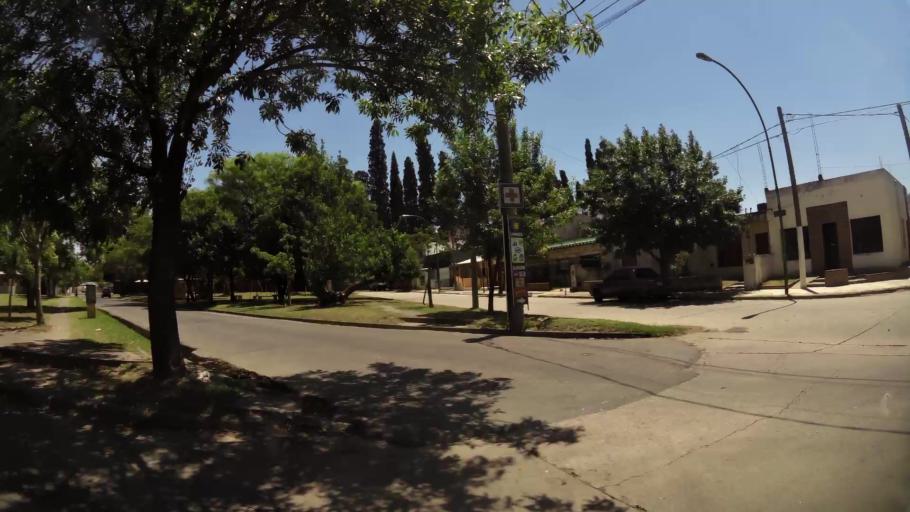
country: AR
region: Cordoba
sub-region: Departamento de Capital
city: Cordoba
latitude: -31.3814
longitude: -64.1419
